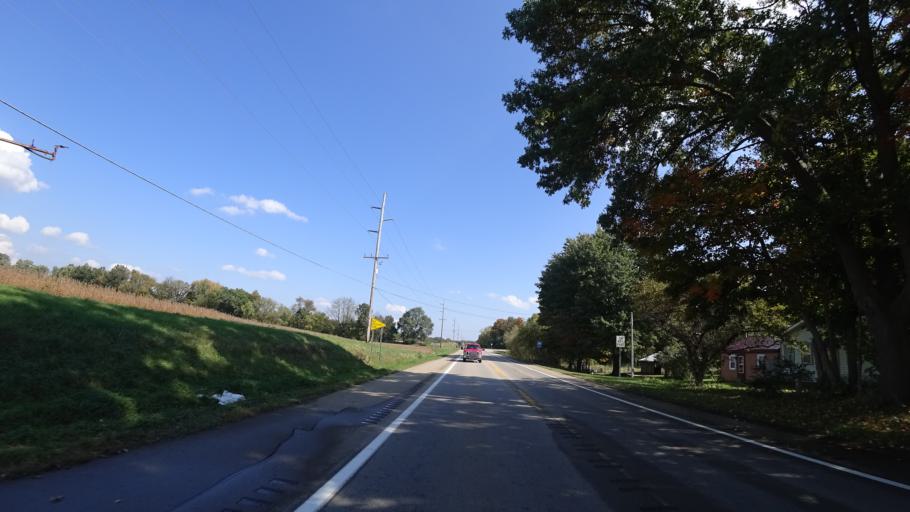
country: US
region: Michigan
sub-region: Jackson County
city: Concord
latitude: 42.1638
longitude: -84.6950
